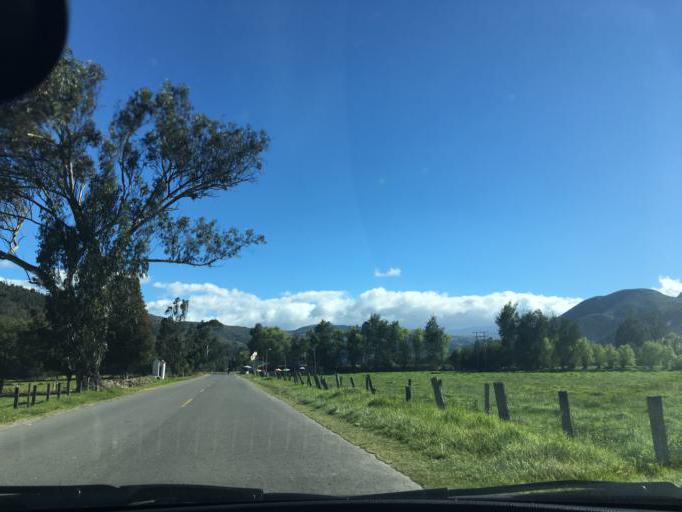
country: CO
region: Boyaca
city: Firavitoba
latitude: 5.6323
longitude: -72.9854
